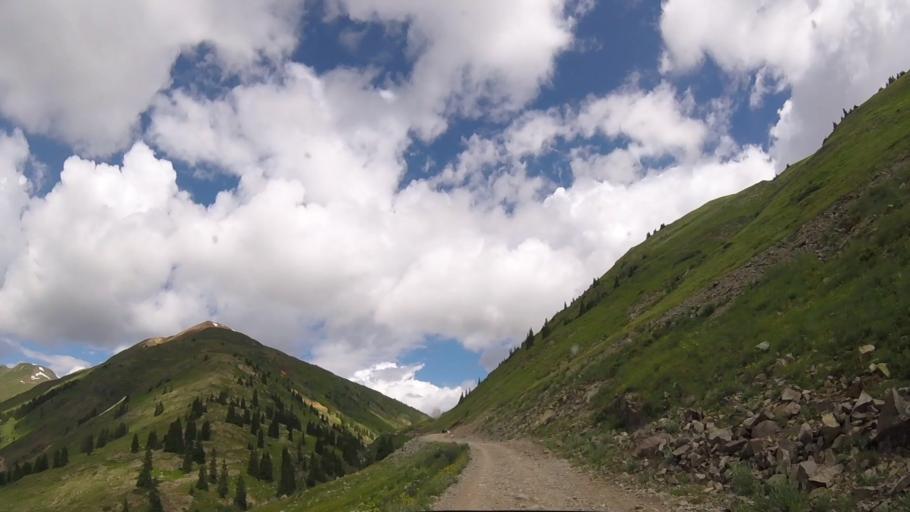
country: US
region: Colorado
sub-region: Ouray County
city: Ouray
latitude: 37.9332
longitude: -107.5682
